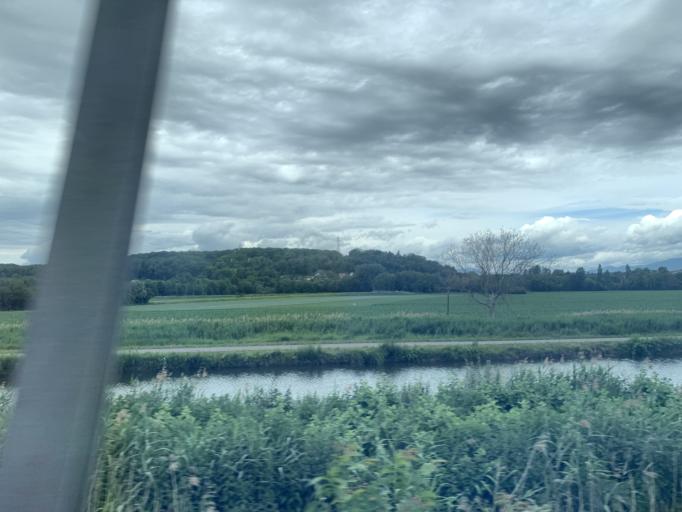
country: FR
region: Alsace
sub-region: Departement du Haut-Rhin
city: Brunstatt
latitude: 47.7123
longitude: 7.3121
